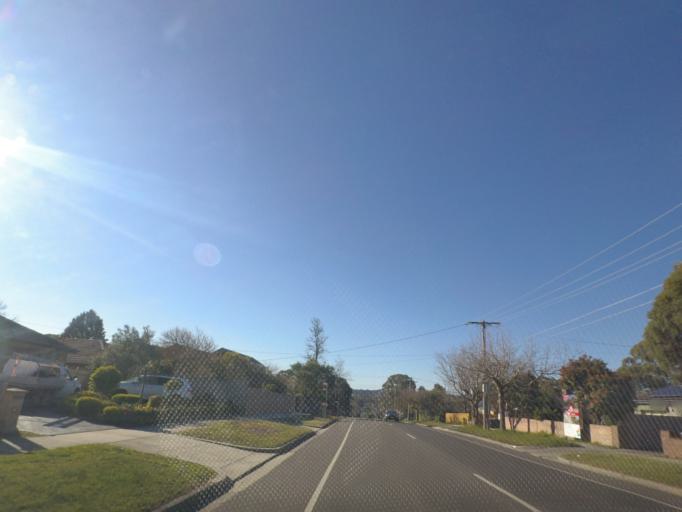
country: AU
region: Victoria
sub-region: Yarra Ranges
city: Kilsyth
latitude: -37.8001
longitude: 145.3127
